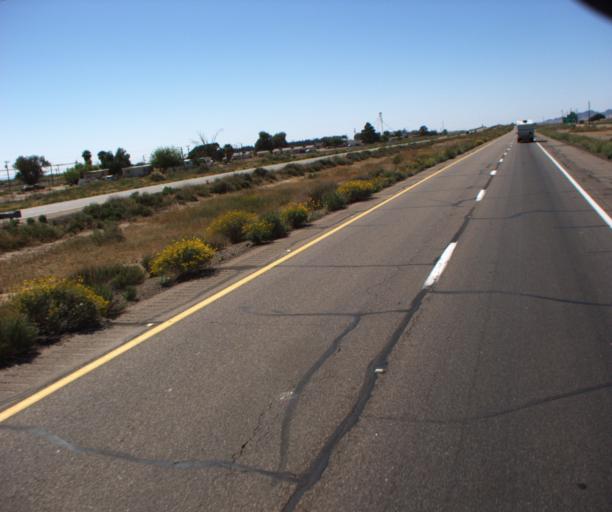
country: US
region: Arizona
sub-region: Maricopa County
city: Gila Bend
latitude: 32.9230
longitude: -112.8799
